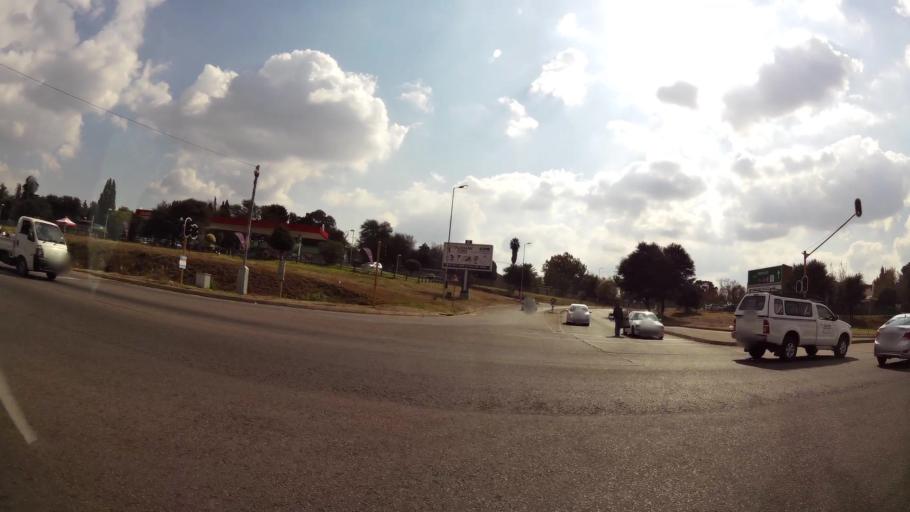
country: ZA
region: Gauteng
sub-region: City of Tshwane Metropolitan Municipality
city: Centurion
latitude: -25.8146
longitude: 28.2778
